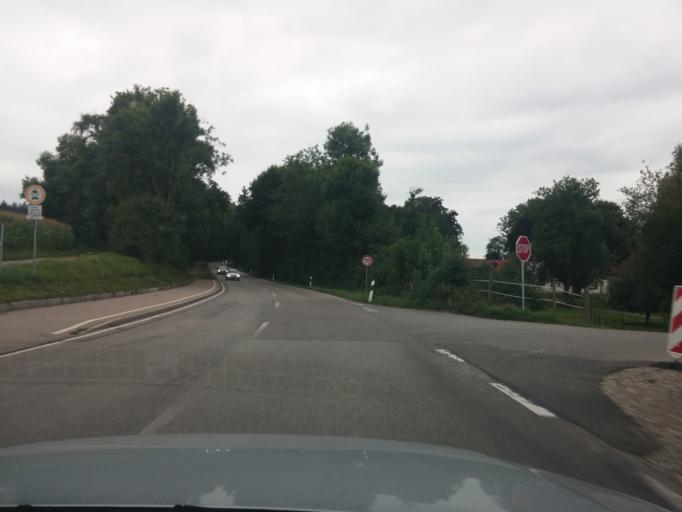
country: DE
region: Baden-Wuerttemberg
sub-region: Tuebingen Region
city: Aitrach
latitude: 47.9501
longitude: 10.1107
